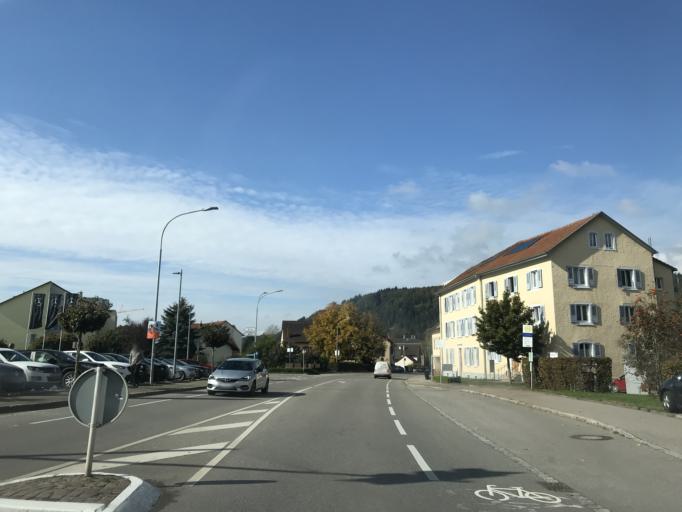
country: DE
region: Baden-Wuerttemberg
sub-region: Freiburg Region
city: Schopfheim
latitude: 47.6475
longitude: 7.8040
